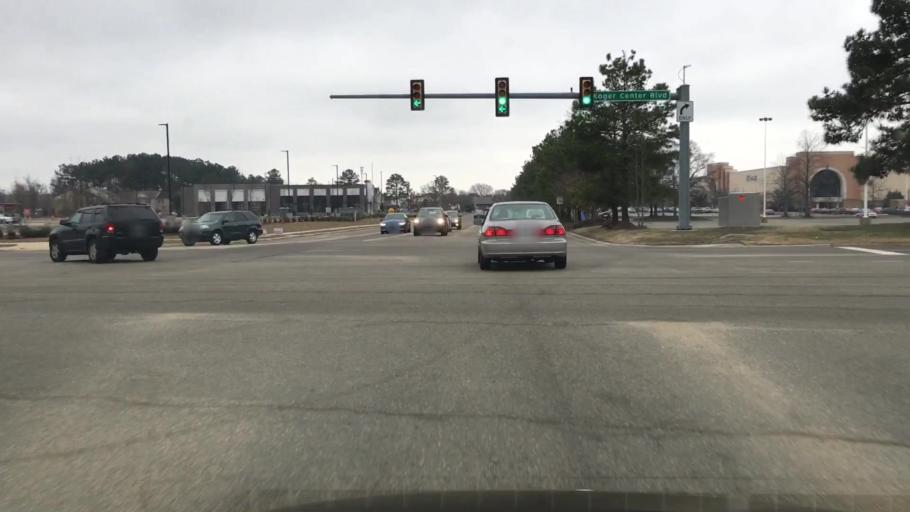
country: US
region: Virginia
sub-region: Chesterfield County
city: Bon Air
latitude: 37.5120
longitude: -77.6070
